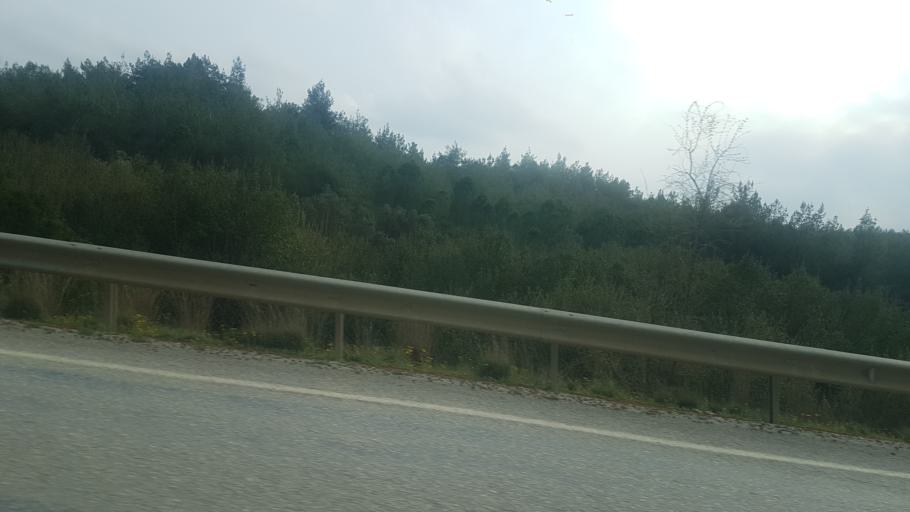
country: TR
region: Mersin
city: Yenice
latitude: 37.0857
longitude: 35.1666
